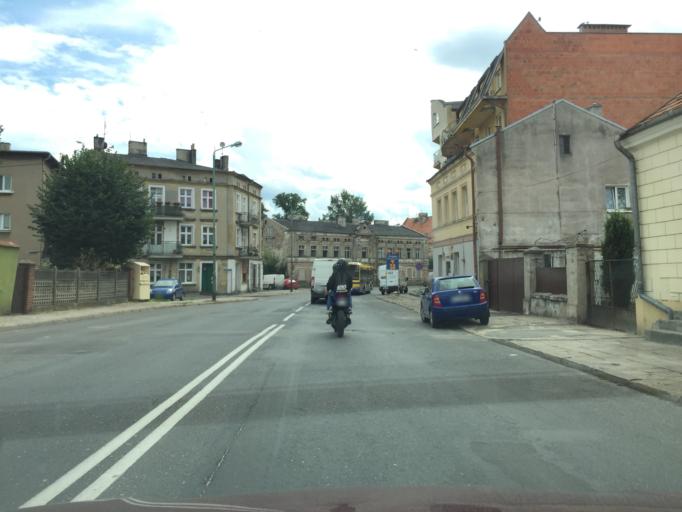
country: PL
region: Greater Poland Voivodeship
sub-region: Kalisz
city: Kalisz
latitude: 51.7686
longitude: 18.0967
